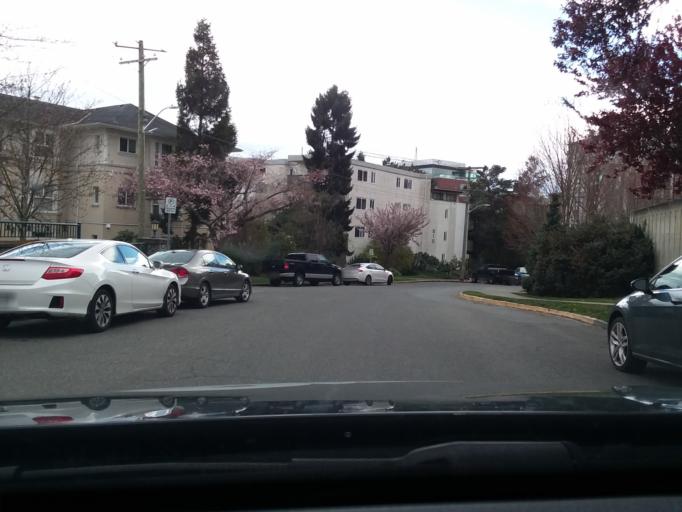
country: CA
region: British Columbia
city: Victoria
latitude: 48.4211
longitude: -123.3610
